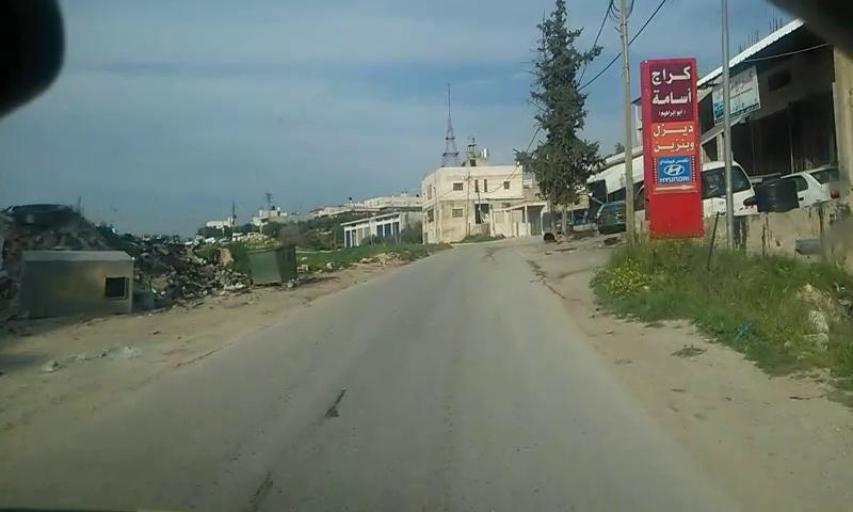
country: PS
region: West Bank
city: Bayt Ula
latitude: 31.6052
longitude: 35.0147
